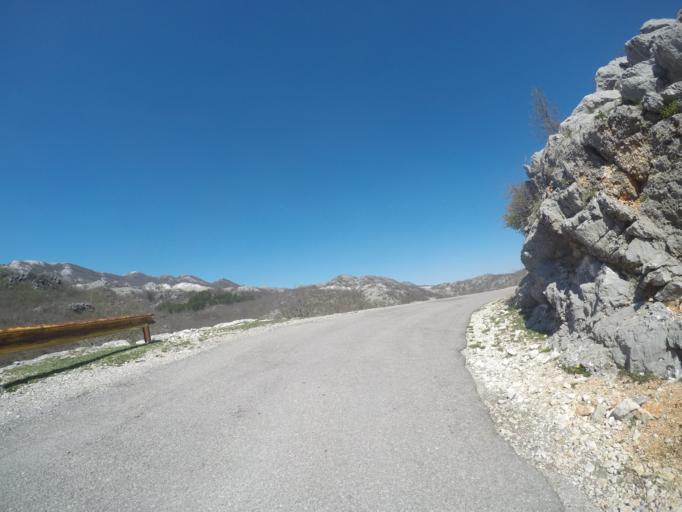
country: ME
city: Dobrota
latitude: 42.4719
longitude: 18.8577
